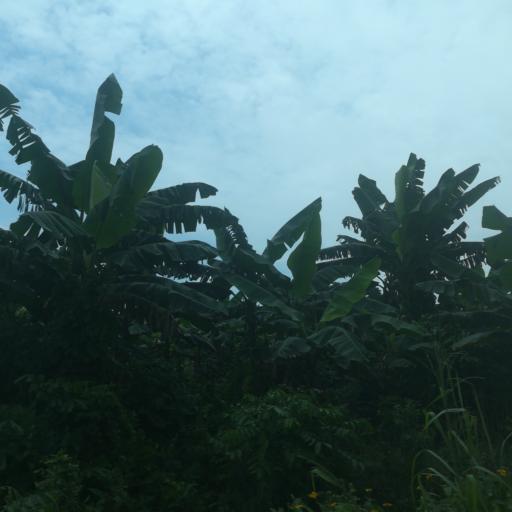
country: NG
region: Lagos
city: Ejirin
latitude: 6.6446
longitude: 3.8496
